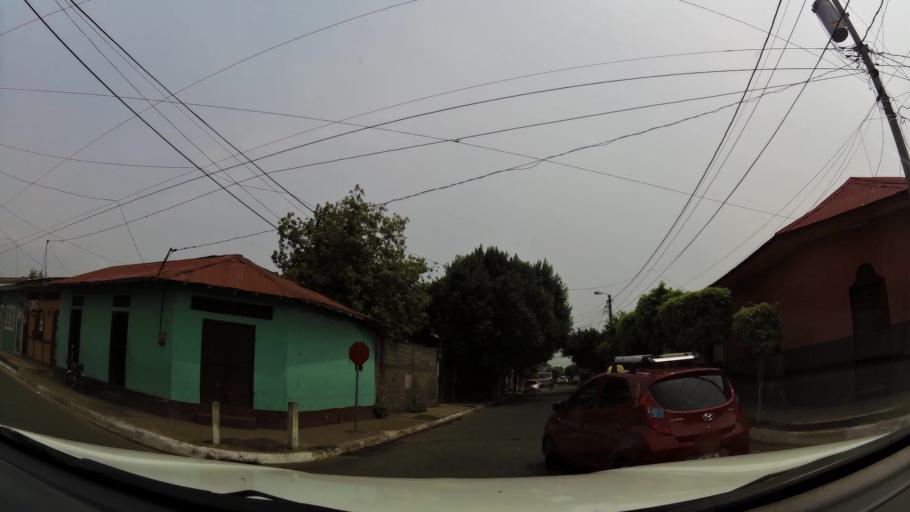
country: NI
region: Chinandega
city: Chinandega
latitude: 12.6271
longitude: -87.1363
